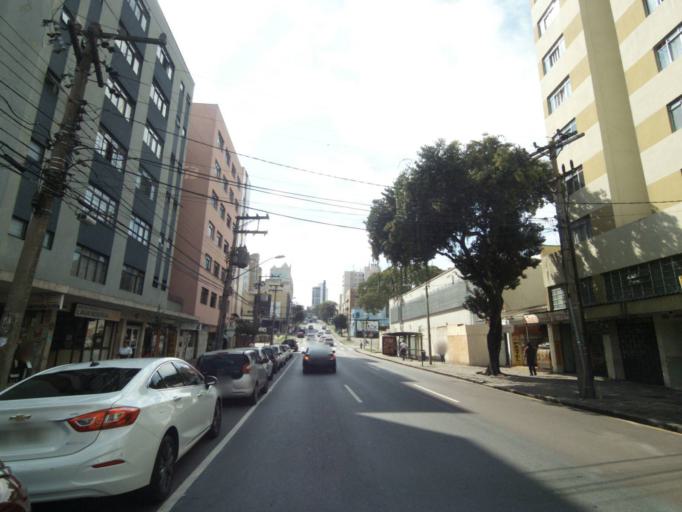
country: BR
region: Parana
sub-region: Curitiba
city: Curitiba
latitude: -25.4315
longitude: -49.2608
